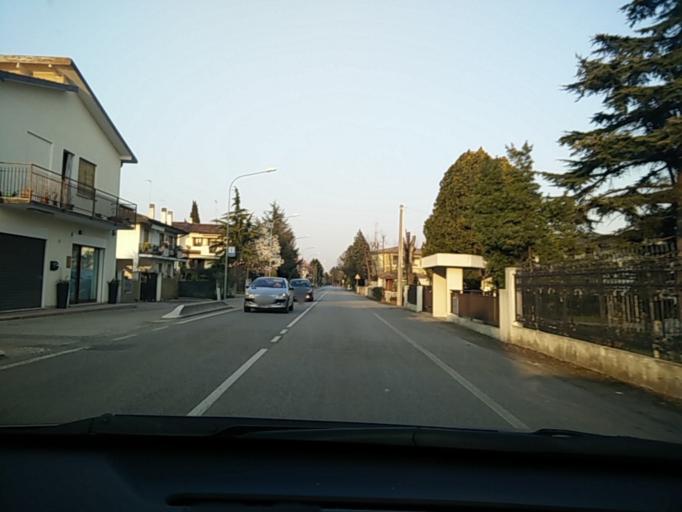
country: IT
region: Veneto
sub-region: Provincia di Venezia
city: Noventa di Piave
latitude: 45.6526
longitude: 12.5227
